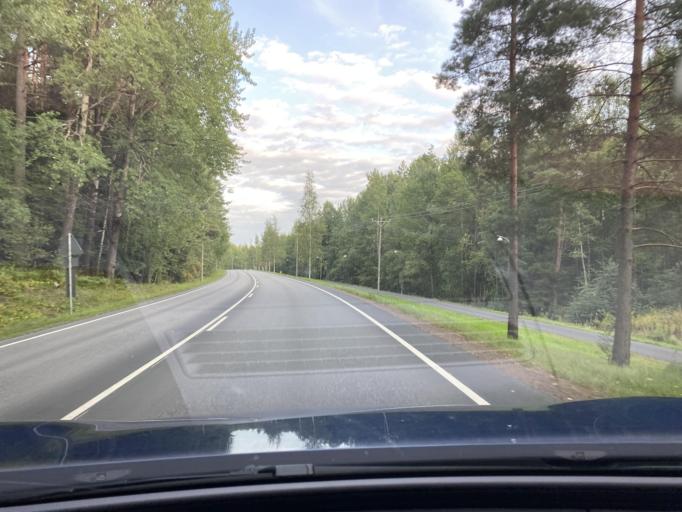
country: FI
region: Kymenlaakso
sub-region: Kouvola
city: Kouvola
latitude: 60.8947
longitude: 26.6766
